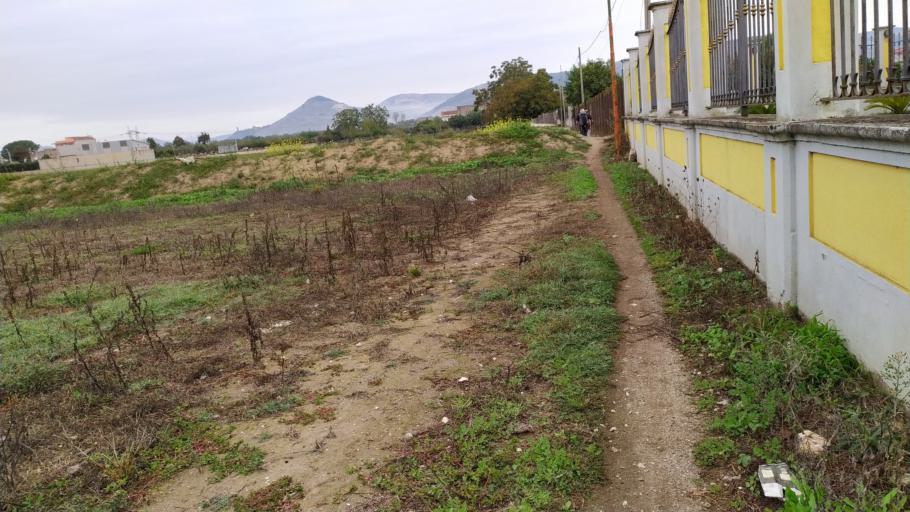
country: IT
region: Campania
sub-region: Provincia di Caserta
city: Montedecoro
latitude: 41.0014
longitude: 14.4139
